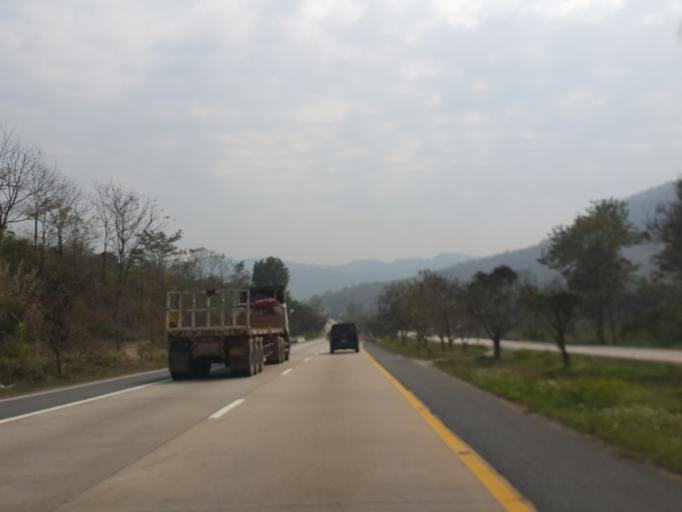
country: TH
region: Lamphun
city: Mae Tha
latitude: 18.4566
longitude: 99.1907
